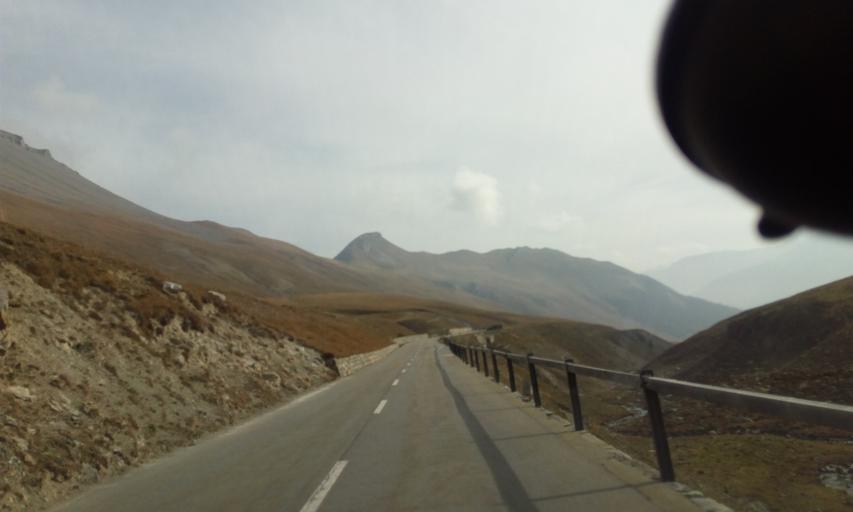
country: CH
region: Grisons
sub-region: Maloja District
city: Ponte
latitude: 46.5882
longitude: 9.8700
